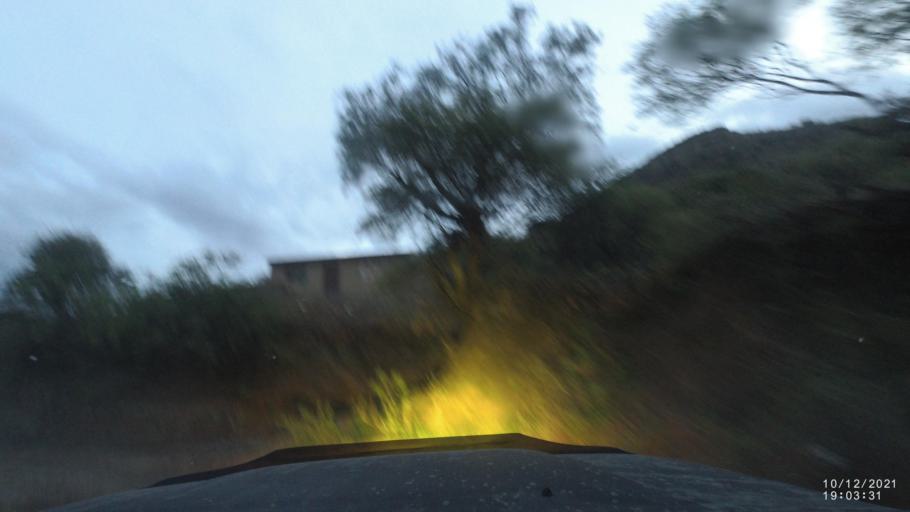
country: BO
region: Cochabamba
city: Tarata
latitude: -17.9011
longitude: -65.9439
